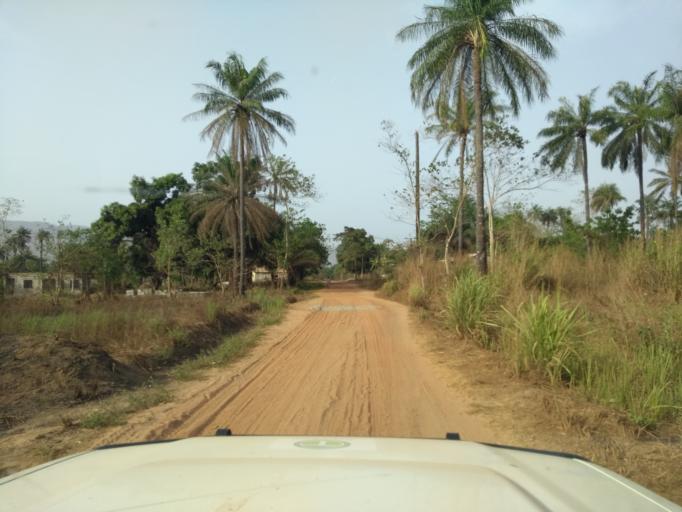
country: GN
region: Kindia
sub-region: Prefecture de Dubreka
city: Dubreka
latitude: 9.8661
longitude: -13.5434
